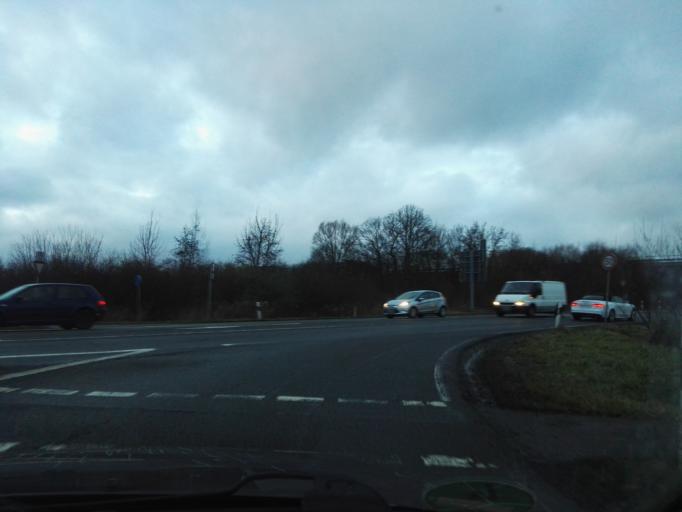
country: DE
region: Lower Saxony
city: Leiferde
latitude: 52.1964
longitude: 10.4571
